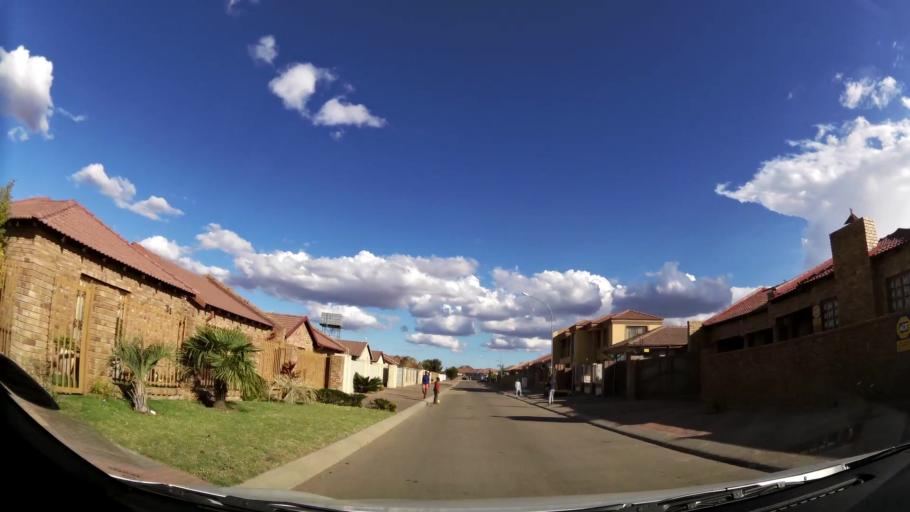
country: ZA
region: Limpopo
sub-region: Capricorn District Municipality
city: Polokwane
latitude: -23.9405
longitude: 29.4436
